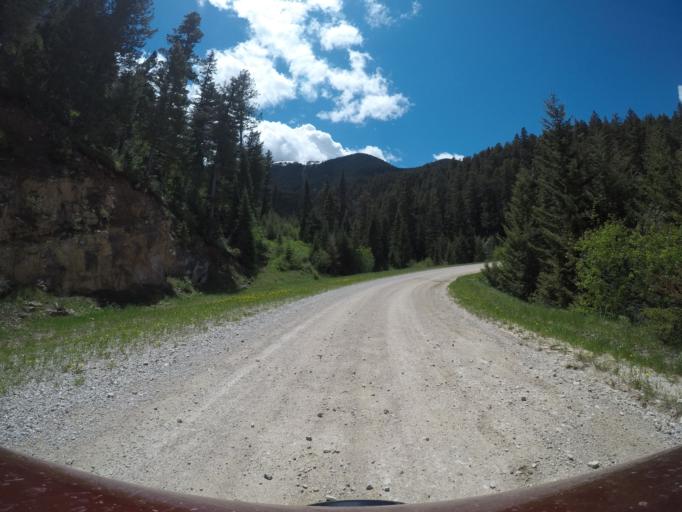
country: US
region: Wyoming
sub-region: Big Horn County
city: Lovell
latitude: 45.1921
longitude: -108.4829
